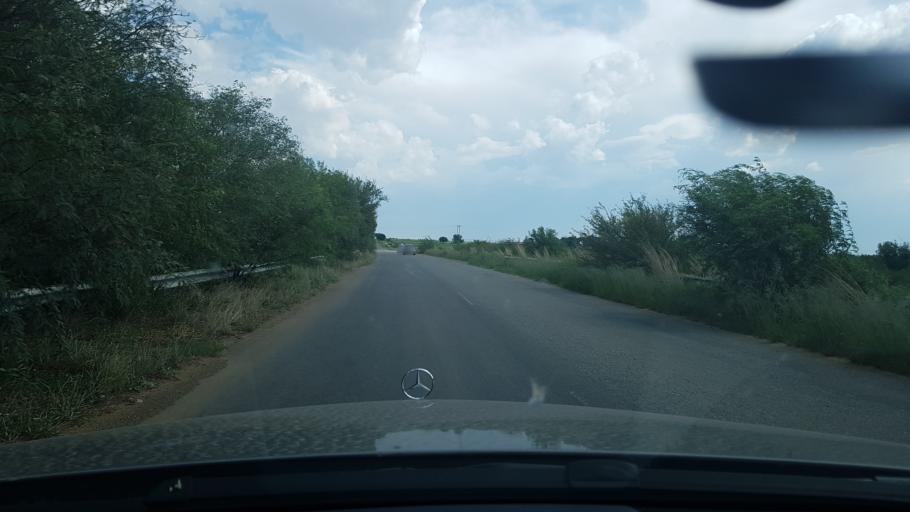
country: ZA
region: North-West
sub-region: Dr Ruth Segomotsi Mompati District Municipality
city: Bloemhof
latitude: -27.6585
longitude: 25.5941
